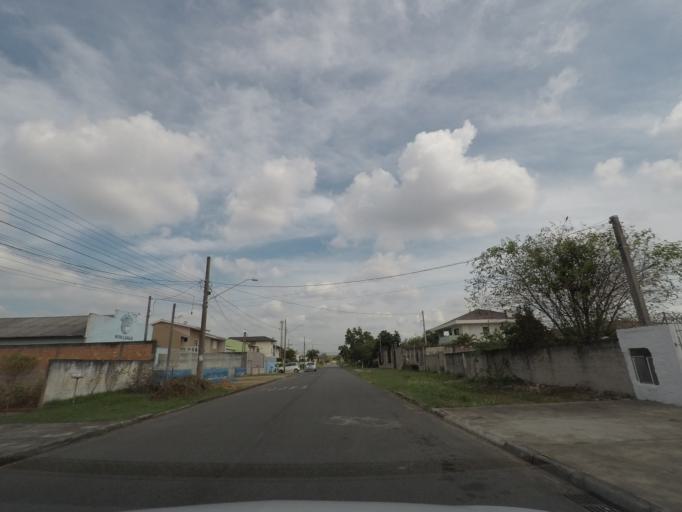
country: BR
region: Parana
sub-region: Pinhais
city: Pinhais
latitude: -25.4758
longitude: -49.1961
